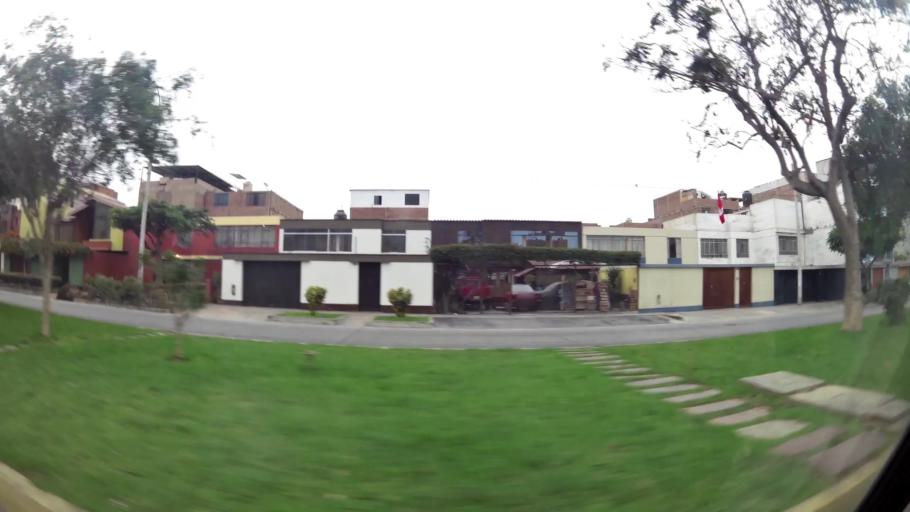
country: PE
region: Lima
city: Lima
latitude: -12.0623
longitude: -77.0658
